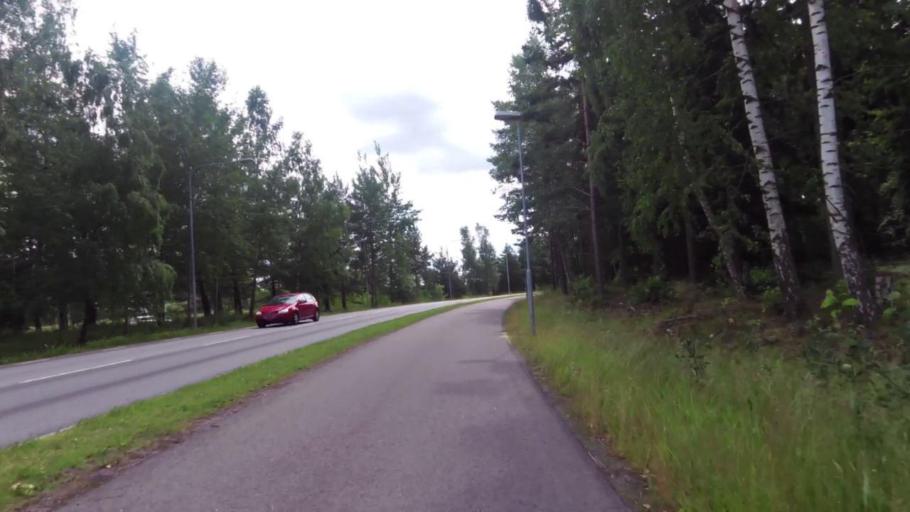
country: SE
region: OEstergoetland
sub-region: Linkopings Kommun
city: Malmslatt
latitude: 58.4026
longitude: 15.5537
